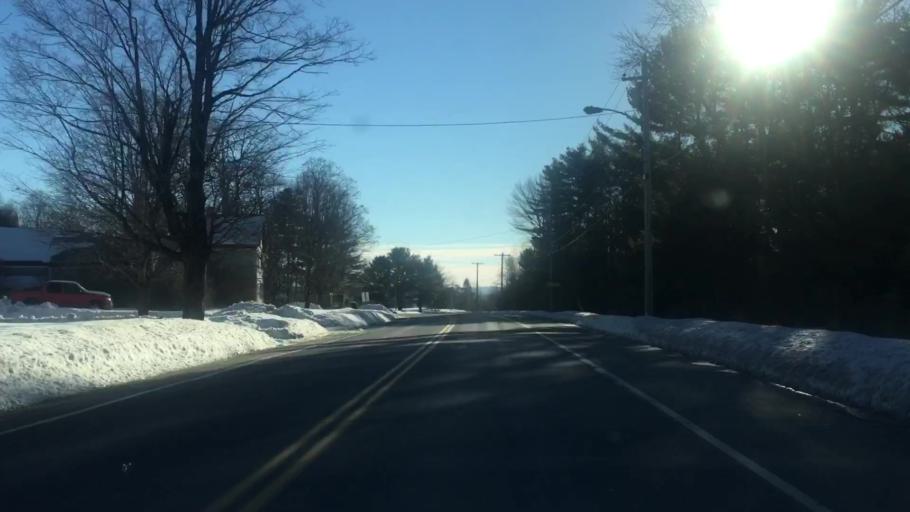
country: US
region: Maine
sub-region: Somerset County
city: Madison
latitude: 44.7845
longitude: -69.8841
